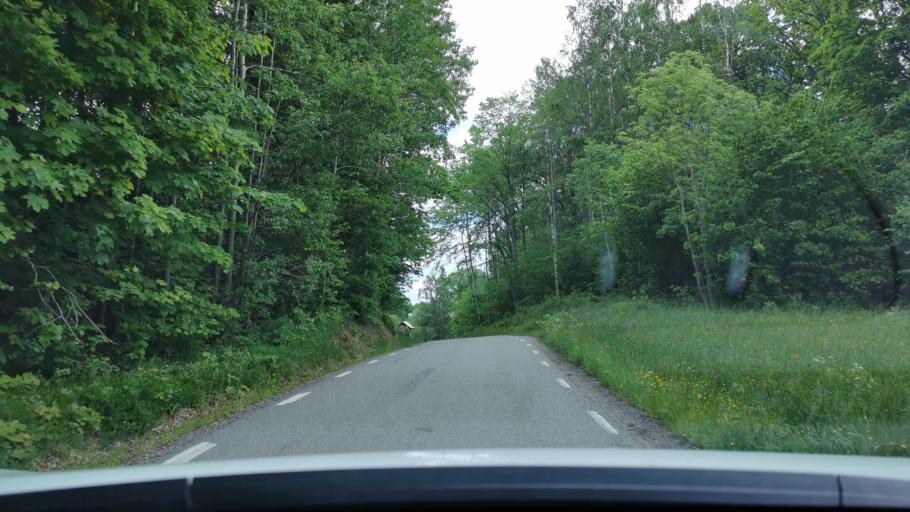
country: SE
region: Vaestra Goetaland
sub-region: Bengtsfors Kommun
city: Dals Langed
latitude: 58.8380
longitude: 12.3300
